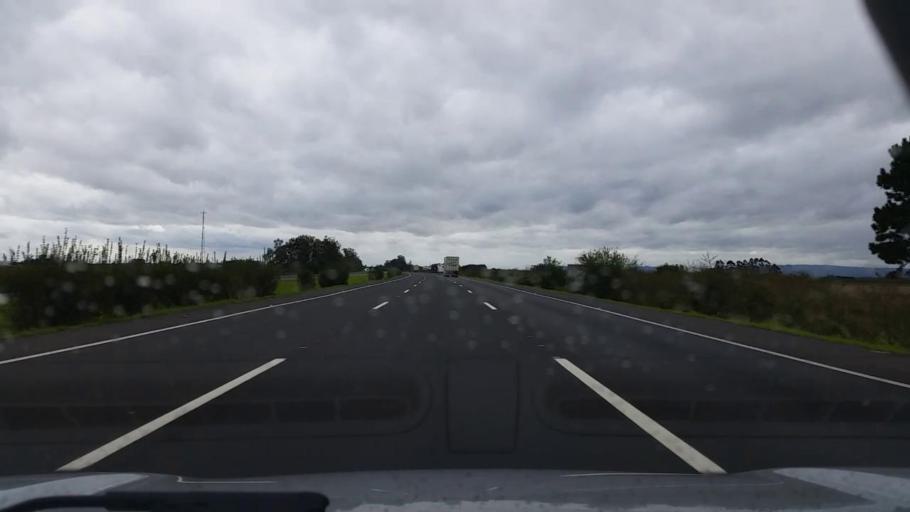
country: BR
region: Rio Grande do Sul
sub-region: Rolante
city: Rolante
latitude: -29.8863
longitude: -50.6606
